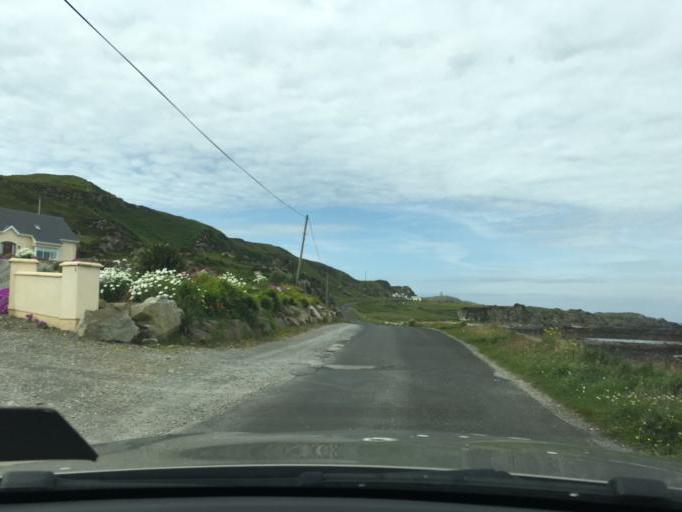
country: IE
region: Ulster
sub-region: County Donegal
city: Carndonagh
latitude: 55.3743
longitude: -7.3467
